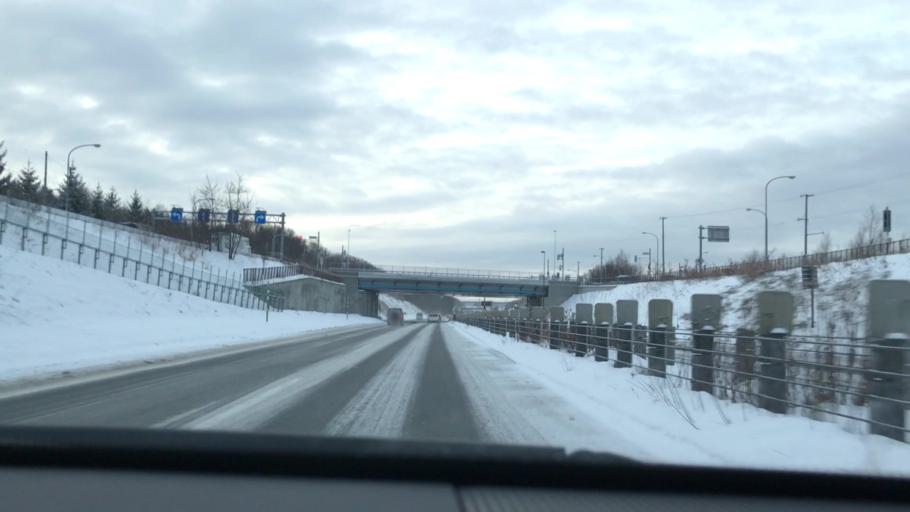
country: JP
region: Hokkaido
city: Kitahiroshima
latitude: 43.0108
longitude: 141.4658
